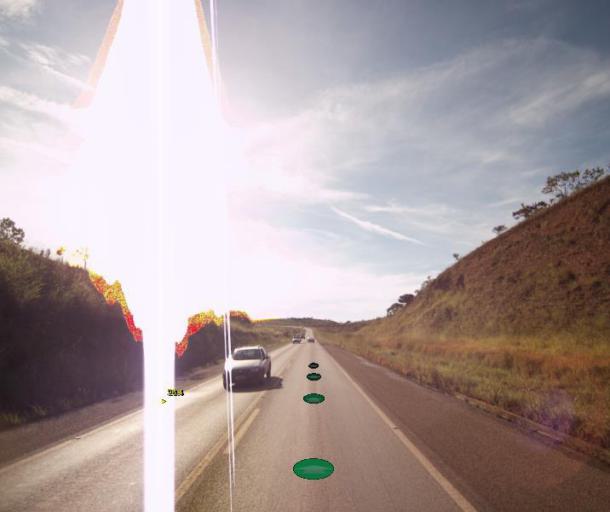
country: BR
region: Federal District
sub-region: Brasilia
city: Brasilia
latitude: -15.7536
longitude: -48.4227
